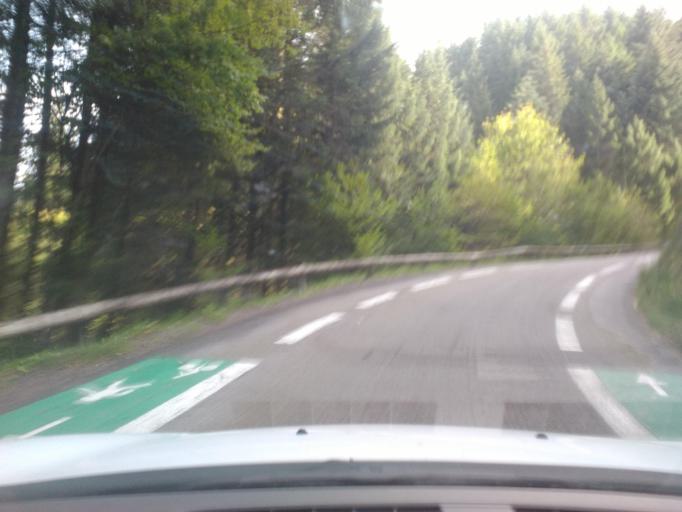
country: FR
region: Lorraine
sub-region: Departement des Vosges
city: Gerardmer
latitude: 48.0591
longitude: 6.8753
